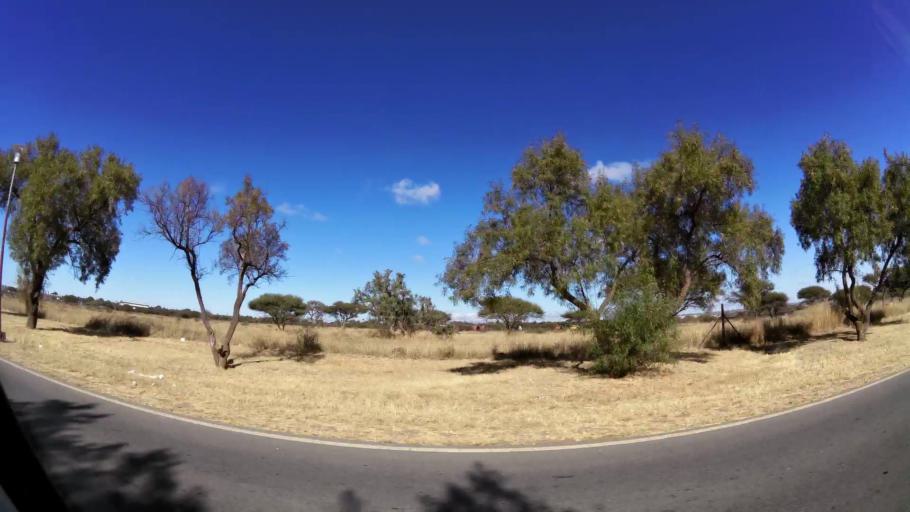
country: ZA
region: Limpopo
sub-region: Capricorn District Municipality
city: Polokwane
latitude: -23.8687
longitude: 29.4627
